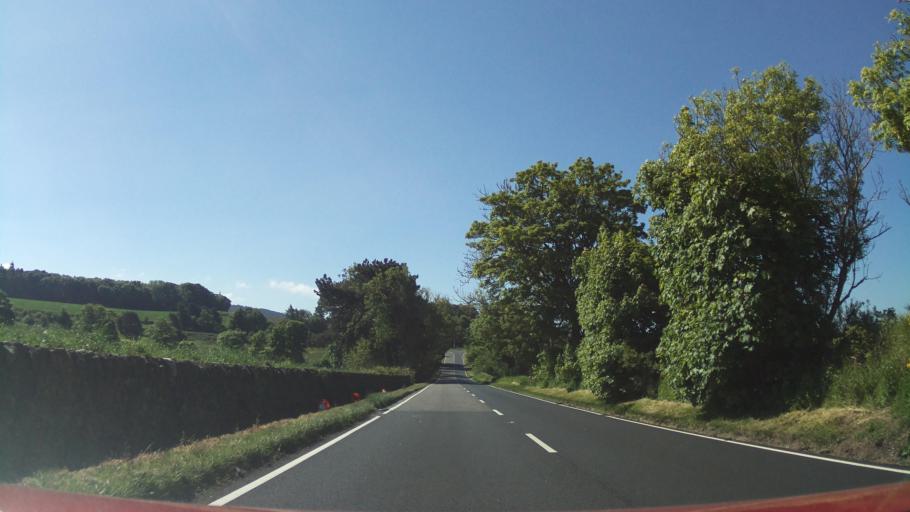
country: GB
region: Scotland
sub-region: Fife
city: Balmullo
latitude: 56.3521
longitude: -2.9415
